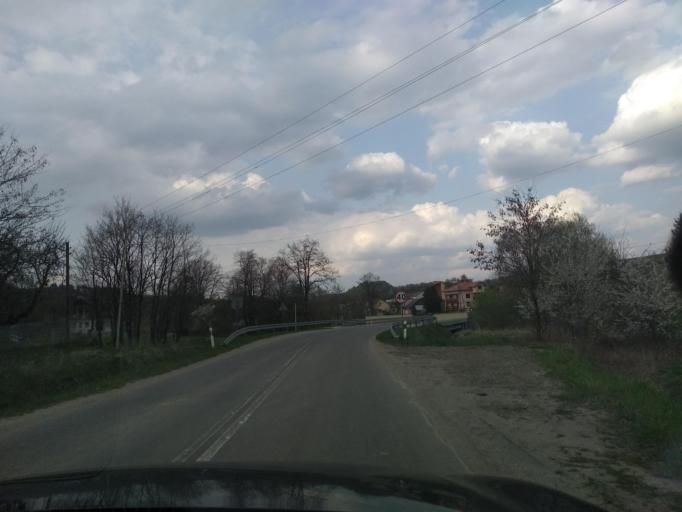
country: PL
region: Subcarpathian Voivodeship
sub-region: Powiat sanocki
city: Czaszyn
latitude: 49.4277
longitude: 22.2402
